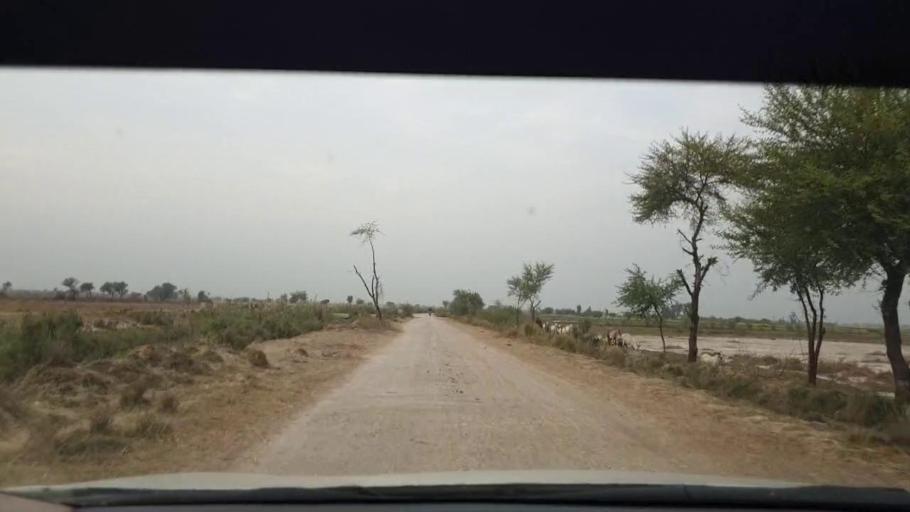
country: PK
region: Sindh
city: Sinjhoro
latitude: 25.9168
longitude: 68.7577
